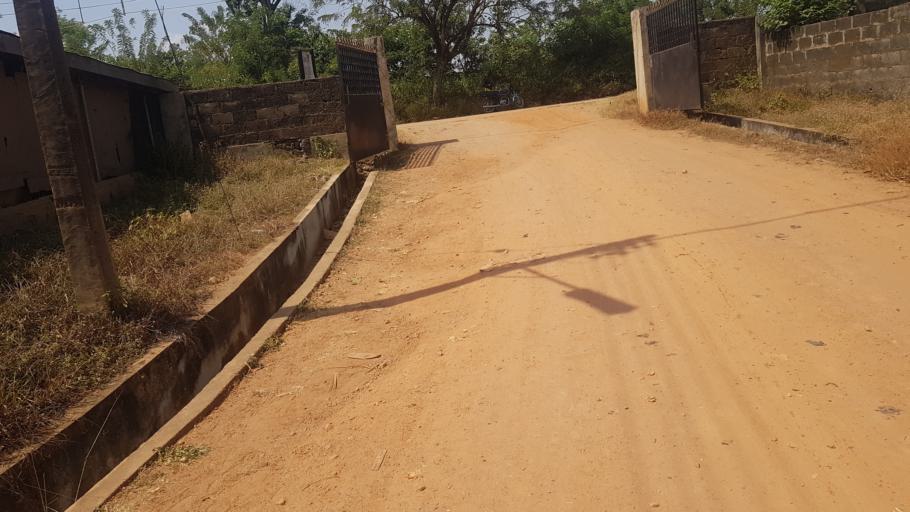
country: NG
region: Osun
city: Osogbo
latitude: 7.7922
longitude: 4.5781
